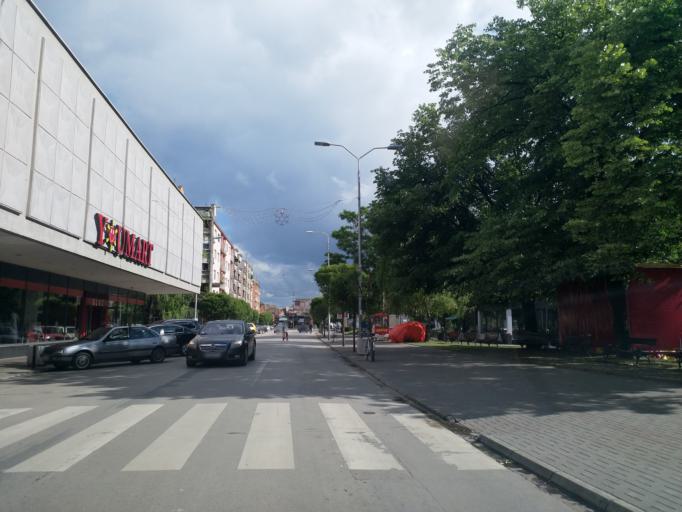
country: RS
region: Central Serbia
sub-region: Pomoravski Okrug
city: Paracin
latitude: 43.8614
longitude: 21.4109
